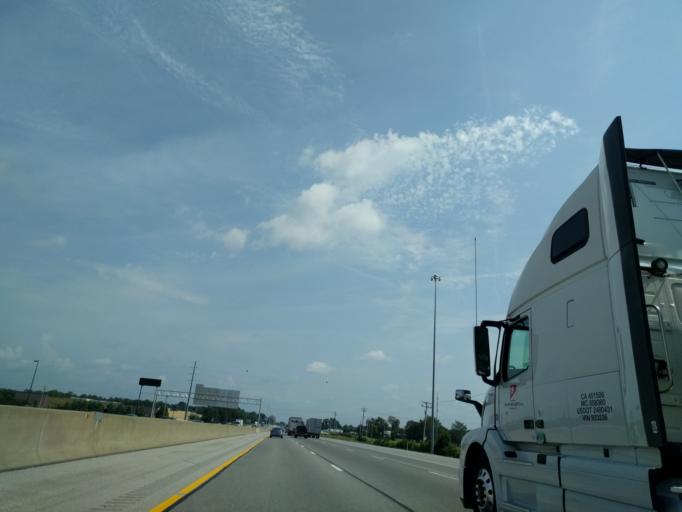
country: US
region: Kentucky
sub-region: Warren County
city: Plano
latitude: 36.9373
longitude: -86.4165
